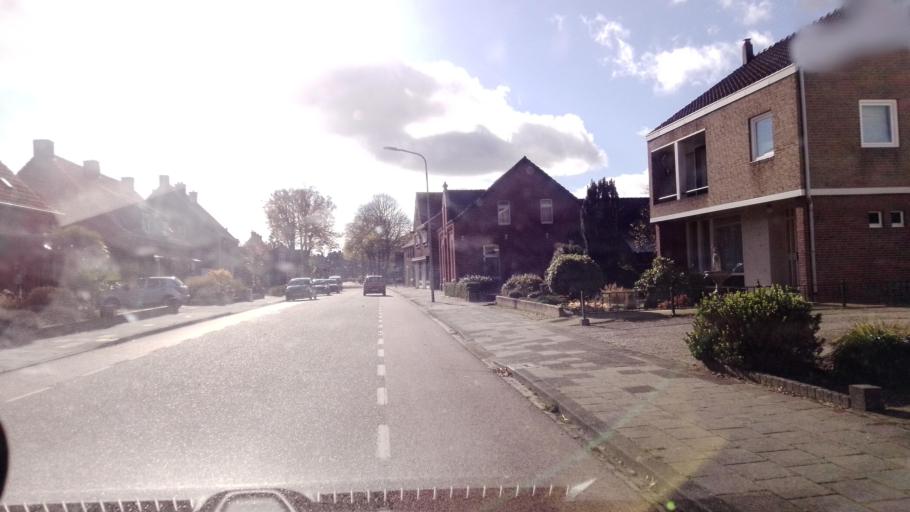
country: NL
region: Limburg
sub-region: Gemeente Venlo
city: Venlo
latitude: 51.4224
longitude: 6.1475
